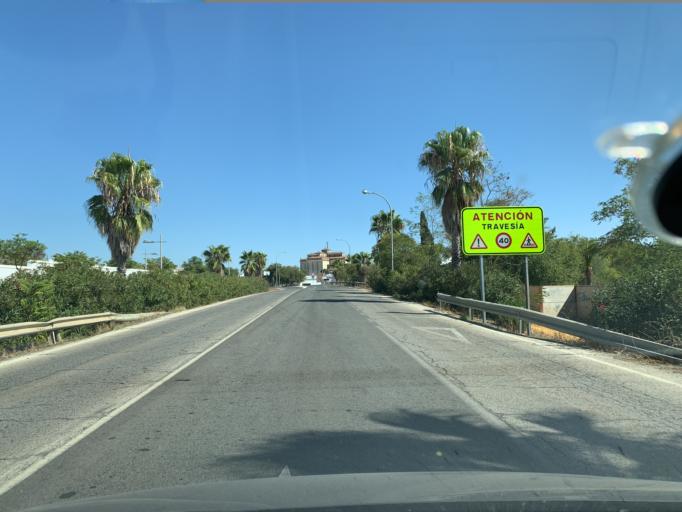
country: ES
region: Andalusia
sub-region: Provincia de Sevilla
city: Carmona
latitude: 37.4661
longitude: -5.6522
